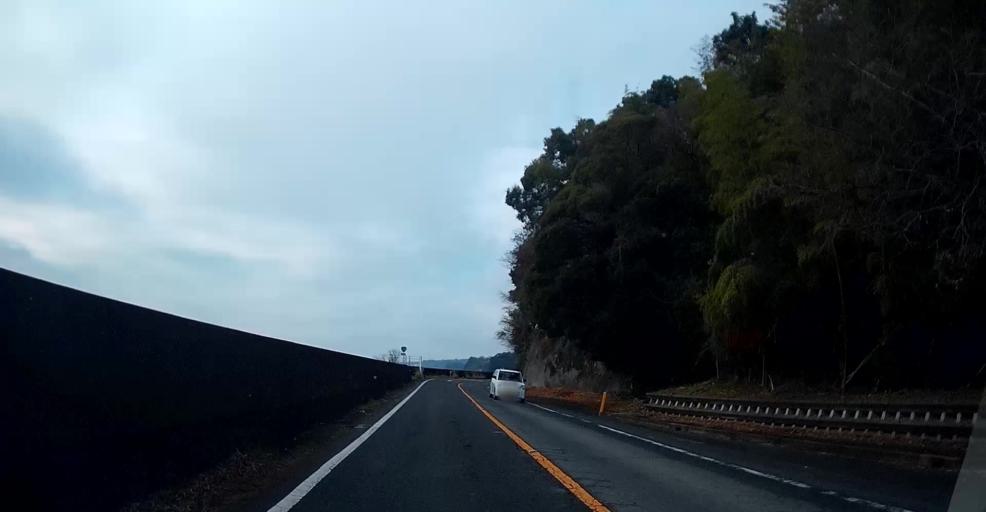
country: JP
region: Kumamoto
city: Matsubase
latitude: 32.6333
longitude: 130.6344
